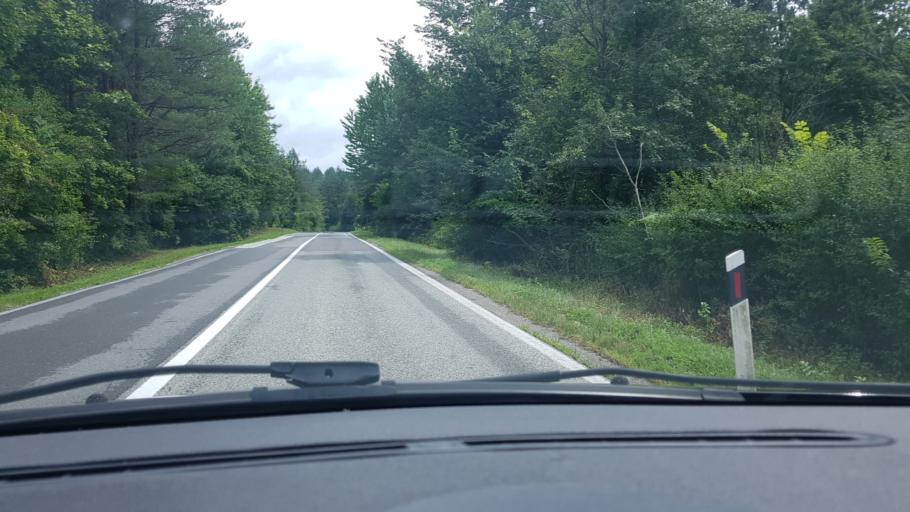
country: HR
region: Licko-Senjska
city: Jezerce
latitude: 44.9386
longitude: 15.6827
